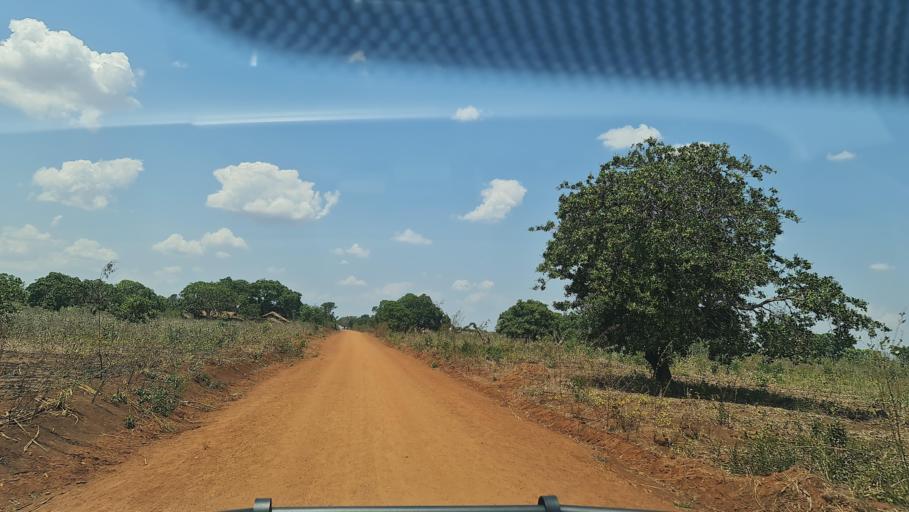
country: MZ
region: Nampula
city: Nacala
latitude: -14.7927
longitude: 40.0668
